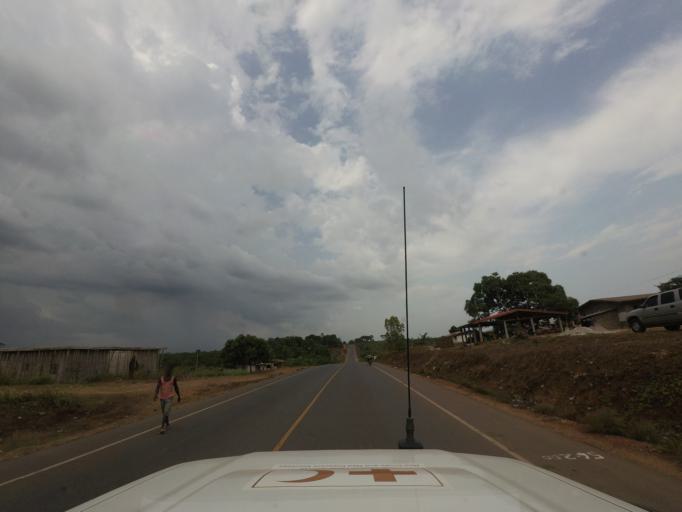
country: LR
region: Margibi
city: Kakata
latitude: 6.5477
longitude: -10.3369
